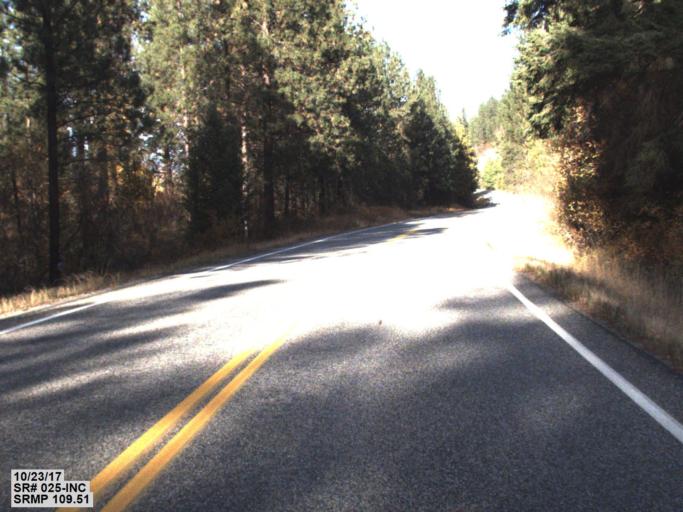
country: CA
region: British Columbia
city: Rossland
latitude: 48.8777
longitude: -117.8378
